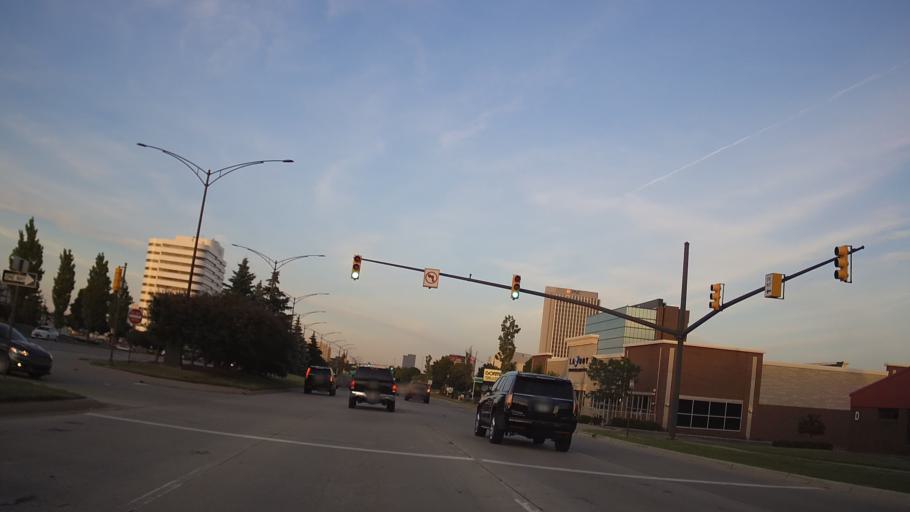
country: US
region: Michigan
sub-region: Oakland County
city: Clawson
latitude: 42.5616
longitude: -83.1704
